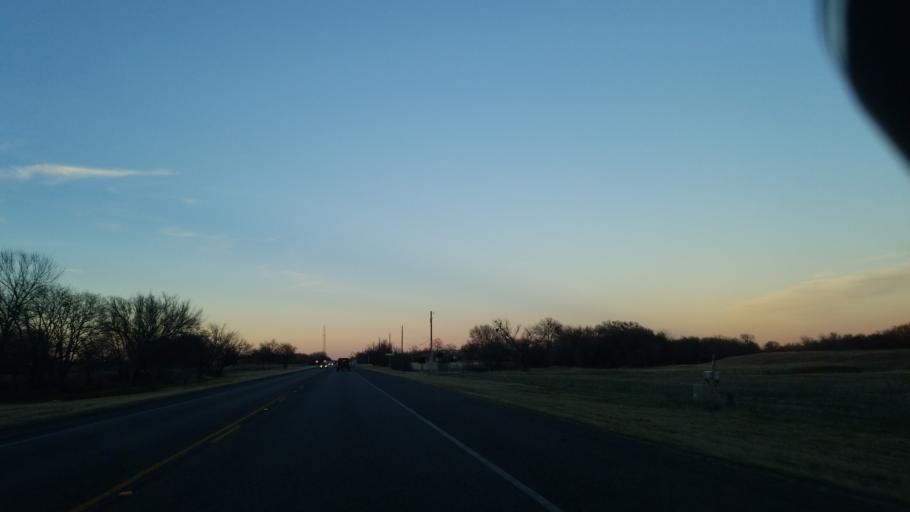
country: US
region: Texas
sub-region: Denton County
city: Argyle
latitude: 33.1298
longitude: -97.1806
